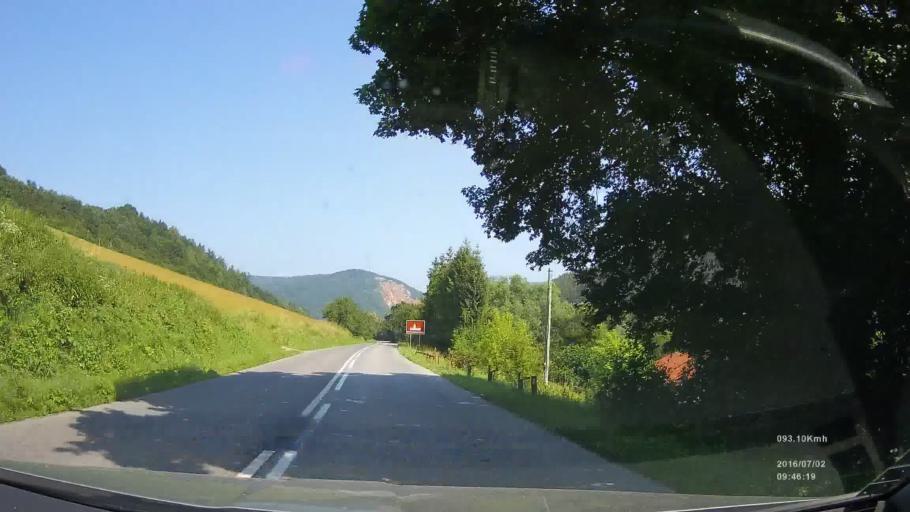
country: SK
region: Kosicky
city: Gelnica
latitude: 48.8619
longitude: 21.0103
